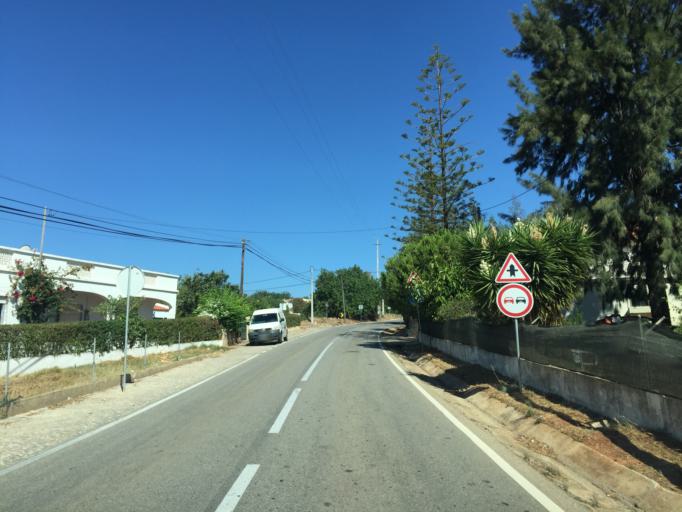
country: PT
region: Faro
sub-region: Loule
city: Vilamoura
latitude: 37.1136
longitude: -8.0907
